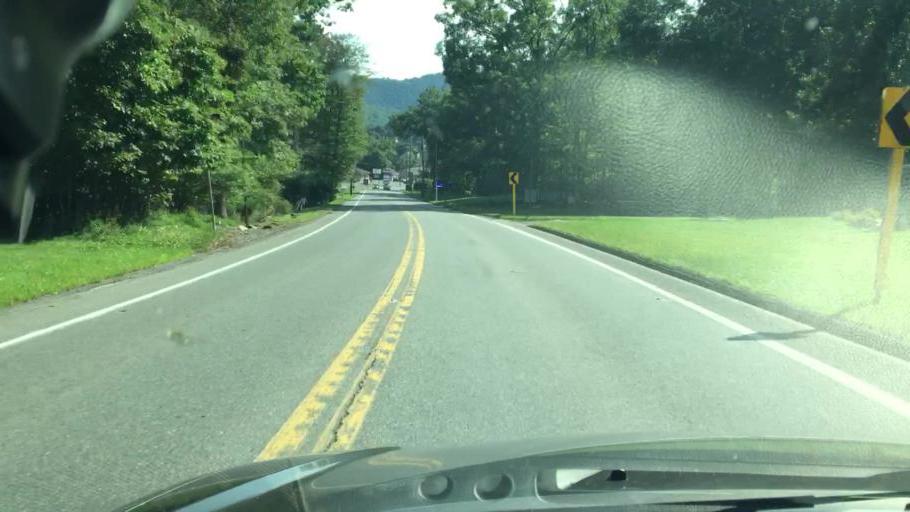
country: US
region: Pennsylvania
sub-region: Carbon County
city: Jim Thorpe
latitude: 40.8847
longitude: -75.7252
